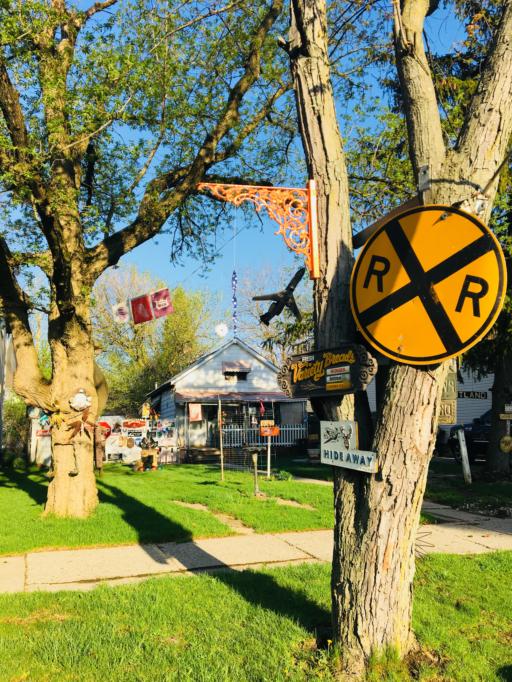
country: US
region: Michigan
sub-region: Wayne County
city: Dearborn Heights
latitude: 42.3336
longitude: -83.2254
